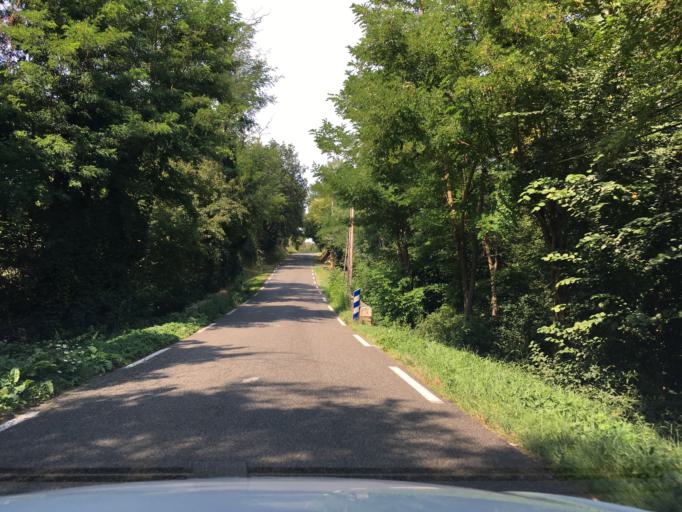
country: FR
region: Midi-Pyrenees
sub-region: Departement du Tarn-et-Garonne
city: Montauban
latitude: 43.9924
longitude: 1.3760
